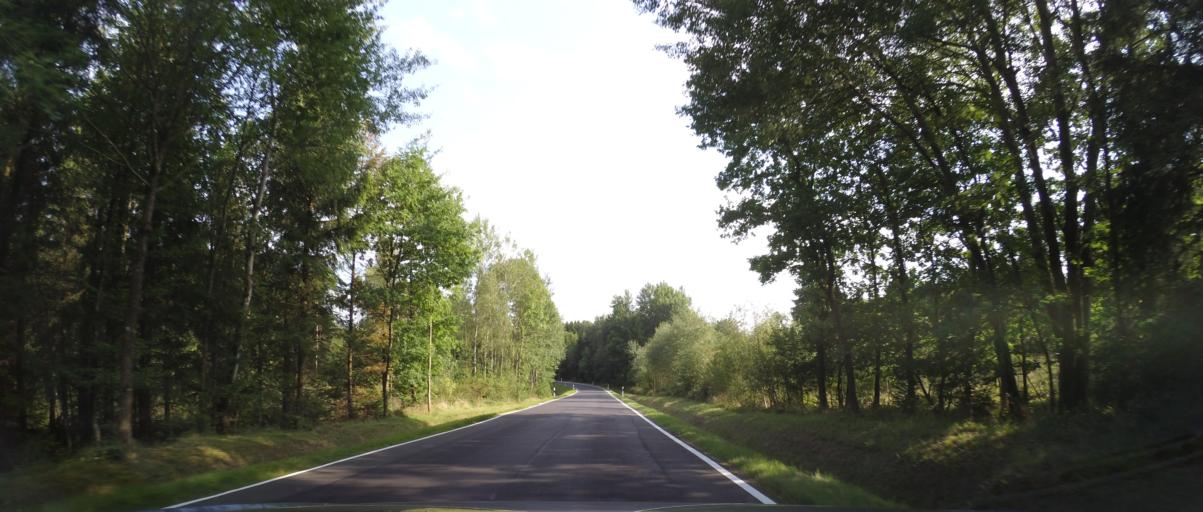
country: DE
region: Rheinland-Pfalz
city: Bongard
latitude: 50.3001
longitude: 6.8196
